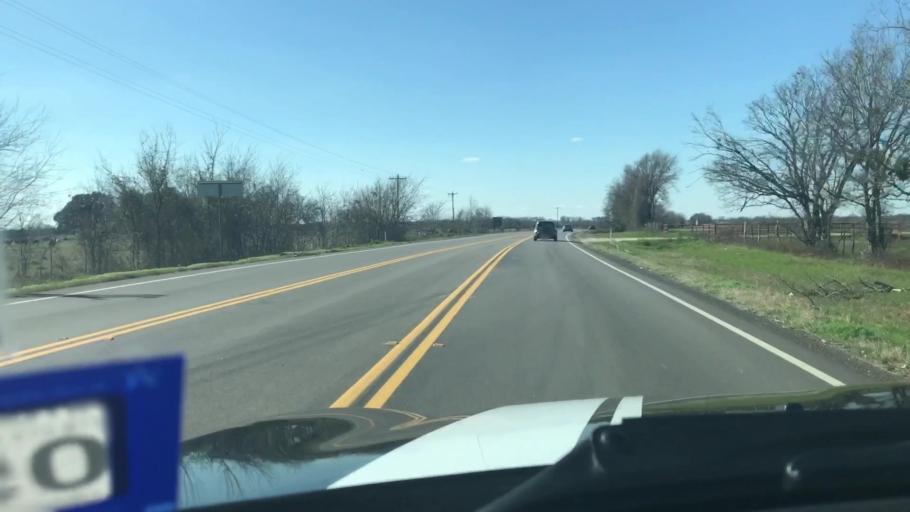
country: US
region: Texas
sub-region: Robertson County
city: Hearne
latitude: 30.8841
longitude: -96.6273
